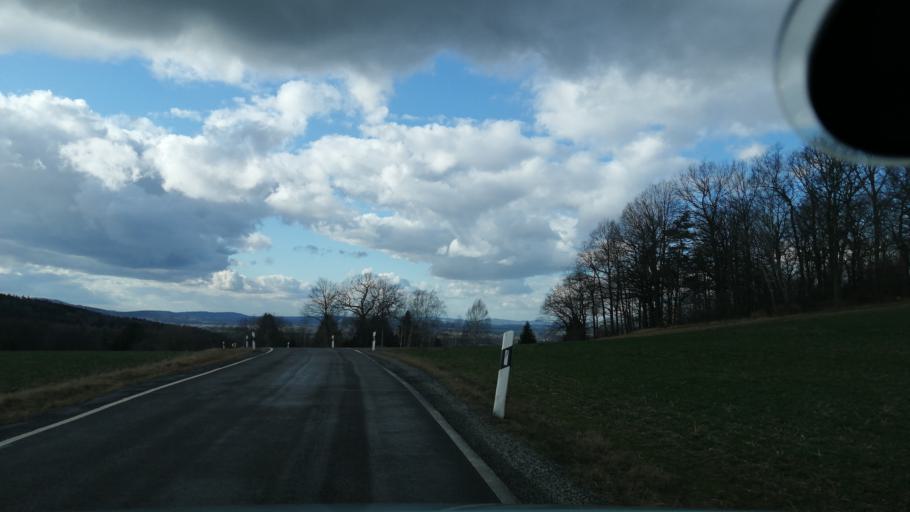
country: DE
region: Saxony
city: Kubschutz
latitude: 51.1399
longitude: 14.4807
